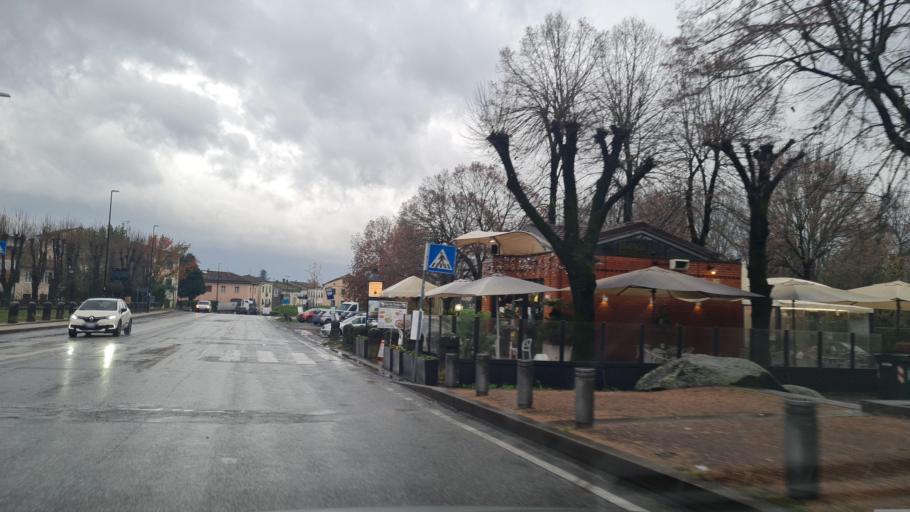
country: IT
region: Tuscany
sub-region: Provincia di Lucca
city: Lucca
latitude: 43.8565
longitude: 10.5077
